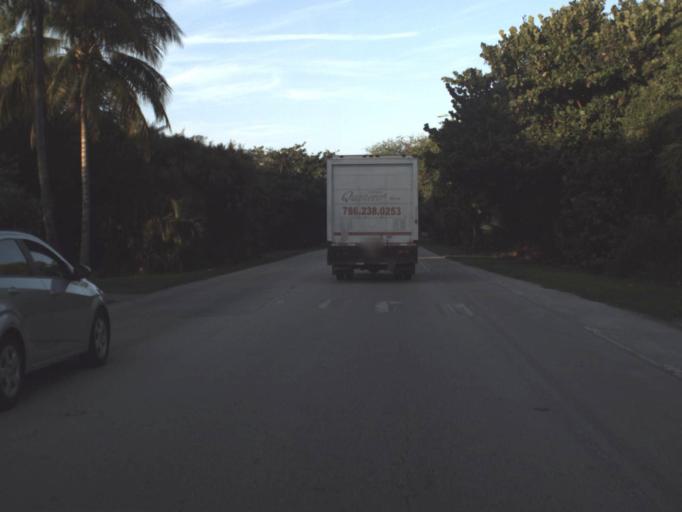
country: US
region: Florida
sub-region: Miami-Dade County
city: Key Biscayne
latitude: 25.7143
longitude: -80.1538
